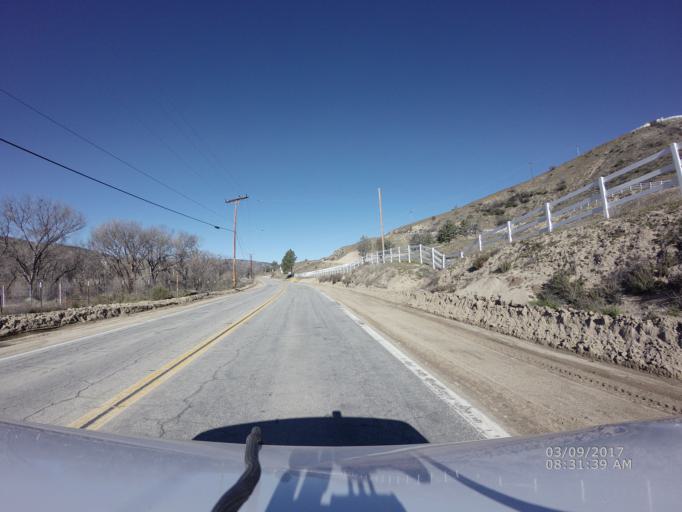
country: US
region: California
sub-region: Los Angeles County
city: Green Valley
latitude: 34.6703
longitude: -118.4193
